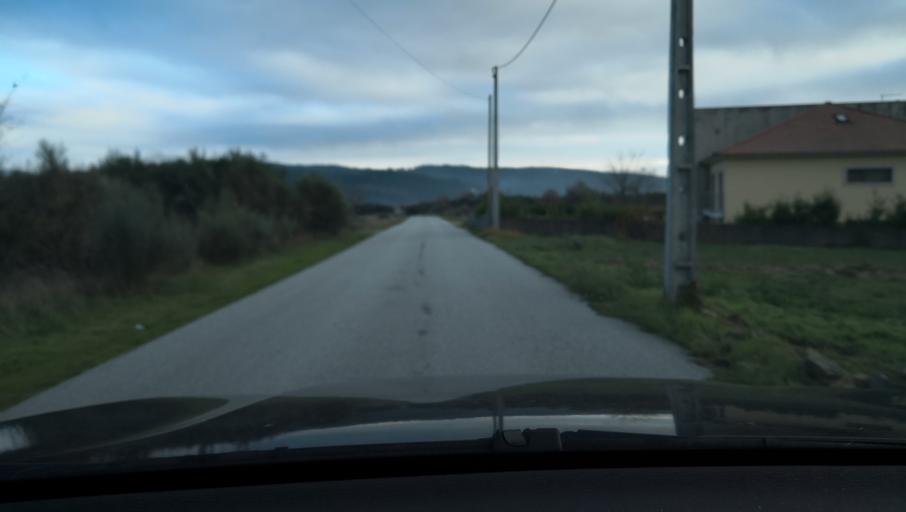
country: PT
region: Vila Real
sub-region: Vila Real
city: Vila Real
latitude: 41.3500
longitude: -7.6649
